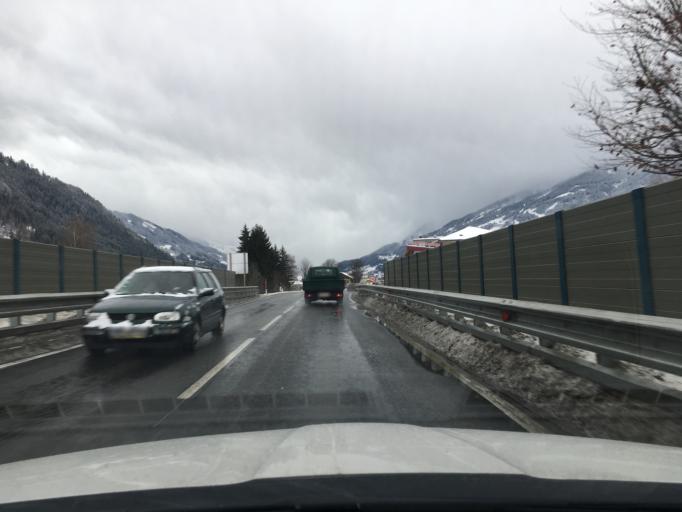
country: AT
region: Tyrol
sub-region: Politischer Bezirk Schwaz
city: Uderns
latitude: 47.3285
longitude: 11.8643
